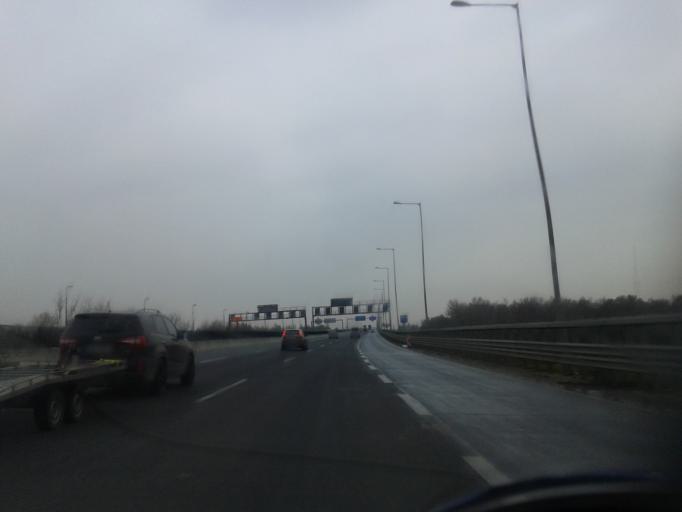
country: HU
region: Budapest
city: Budapest XXII. keruelet
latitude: 47.3967
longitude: 19.0114
